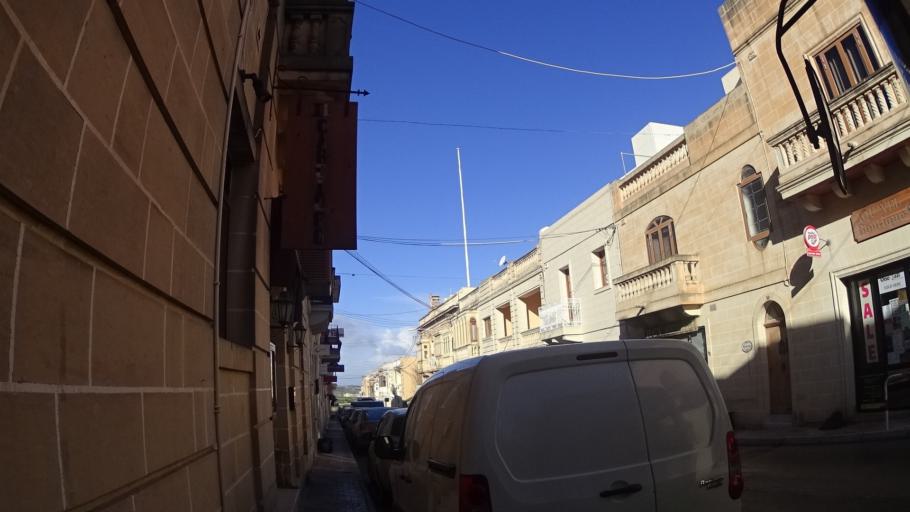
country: MT
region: Hal Gharghur
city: Hal Gharghur
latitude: 35.9239
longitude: 14.4529
